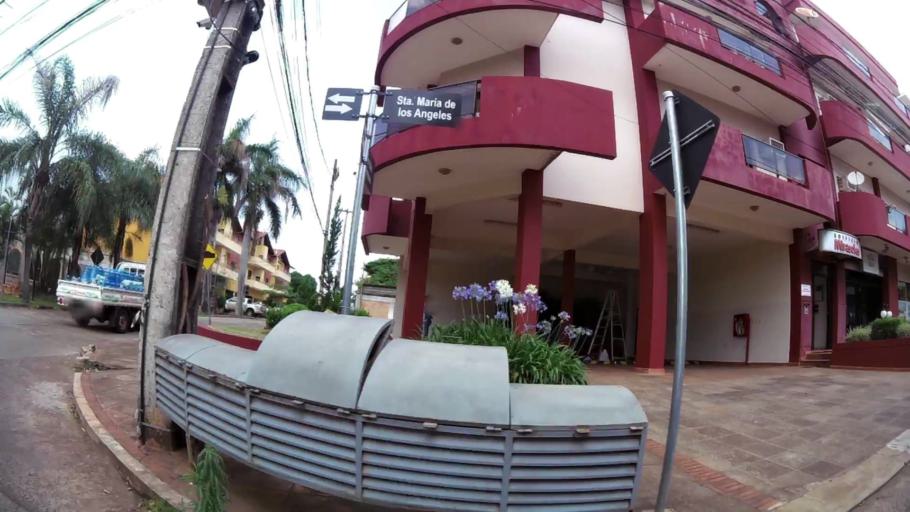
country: PY
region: Alto Parana
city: Ciudad del Este
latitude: -25.4775
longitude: -54.6221
